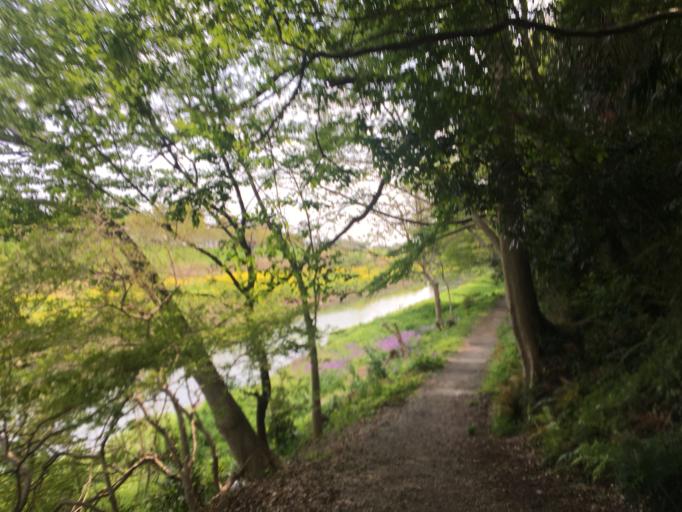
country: JP
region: Saitama
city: Kamifukuoka
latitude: 35.8826
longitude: 139.5256
